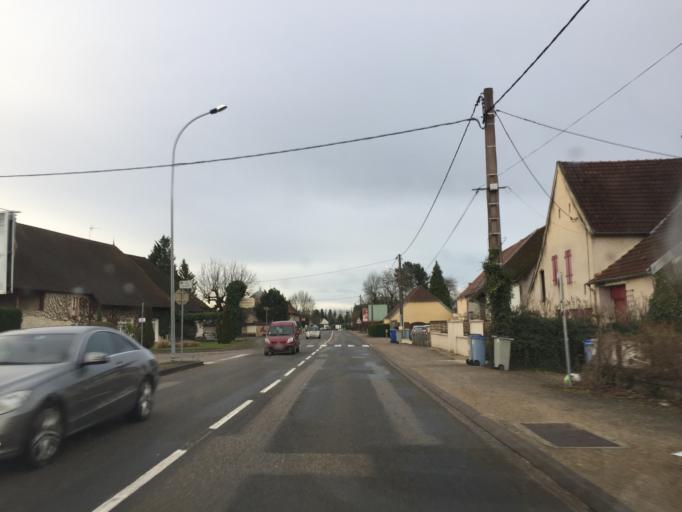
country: FR
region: Franche-Comte
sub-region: Departement du Jura
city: Dole
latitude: 47.0658
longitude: 5.4949
